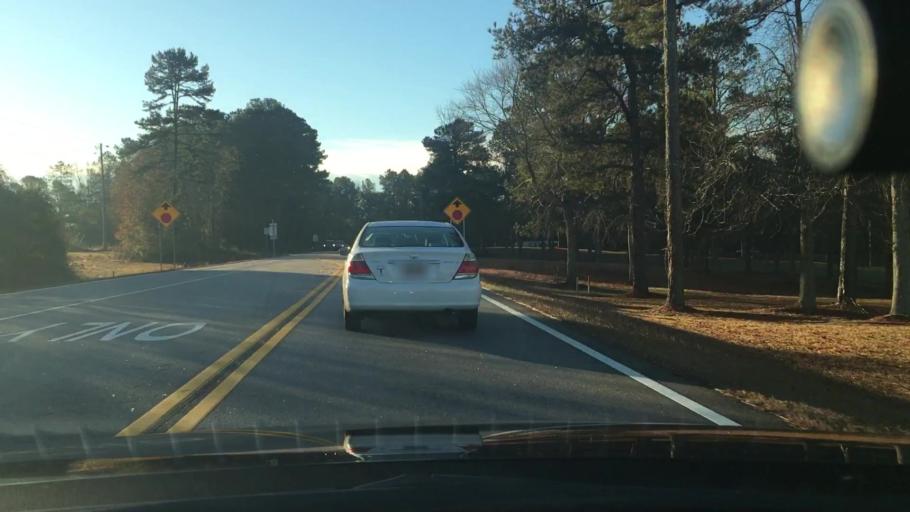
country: US
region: Georgia
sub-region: Fayette County
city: Peachtree City
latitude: 33.3465
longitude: -84.6559
